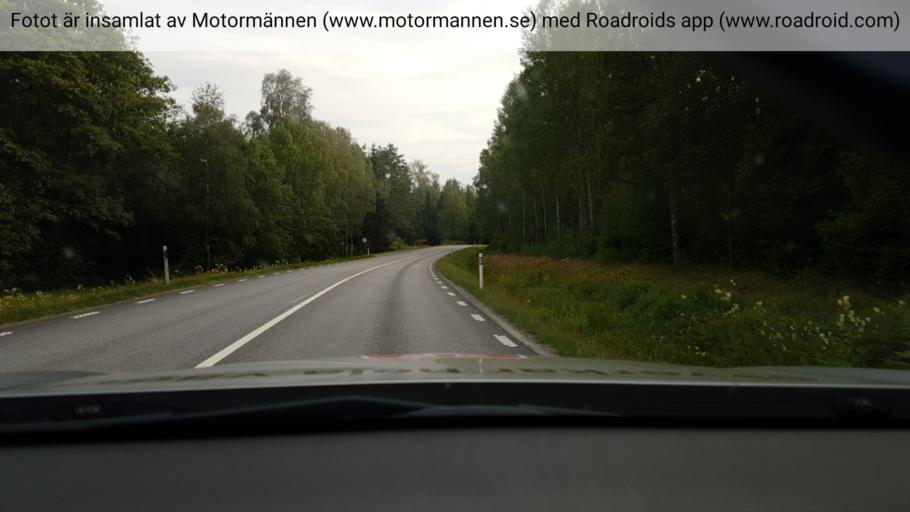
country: SE
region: Vaestra Goetaland
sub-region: Uddevalla Kommun
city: Uddevalla
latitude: 58.4022
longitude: 11.9992
